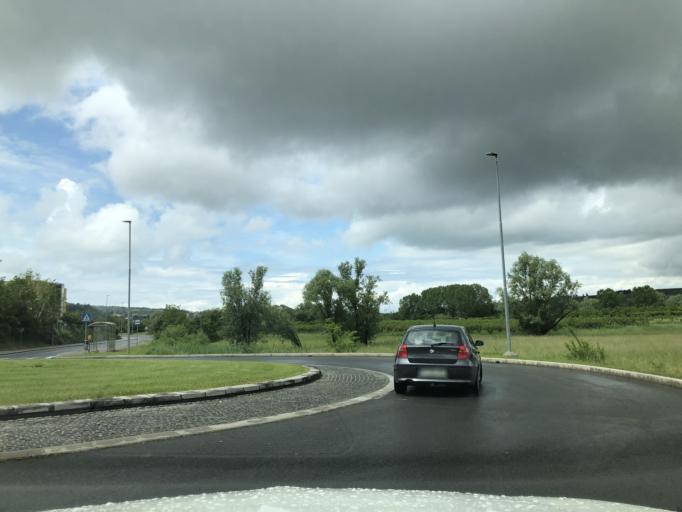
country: SI
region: Koper-Capodistria
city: Koper
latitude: 45.5197
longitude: 13.7478
